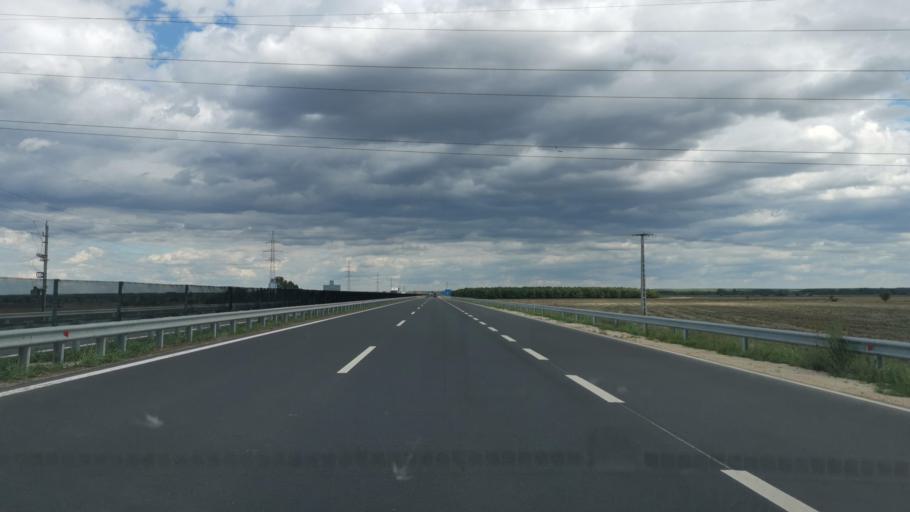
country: HU
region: Jasz-Nagykun-Szolnok
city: Szolnok
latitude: 47.2233
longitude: 20.2222
